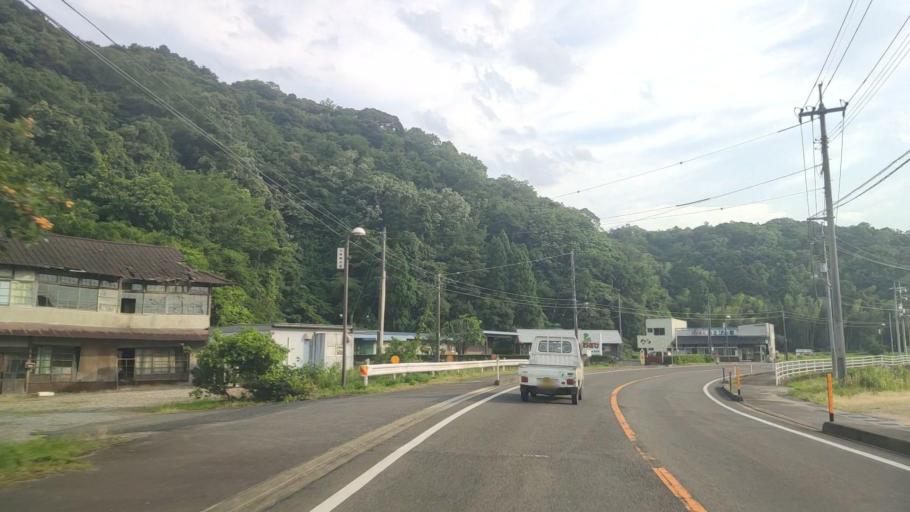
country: JP
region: Tottori
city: Kurayoshi
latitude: 35.3698
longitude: 133.7670
